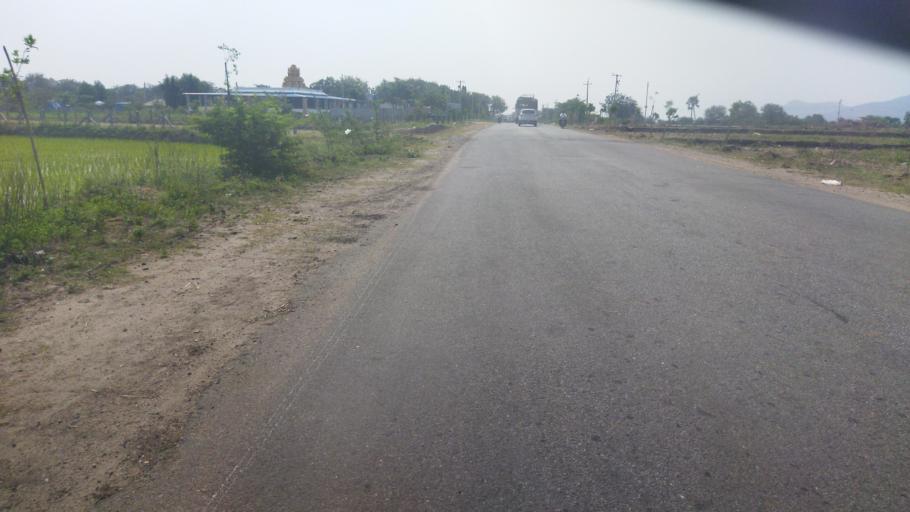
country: IN
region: Telangana
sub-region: Nalgonda
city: Nalgonda
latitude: 17.0971
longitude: 79.2858
